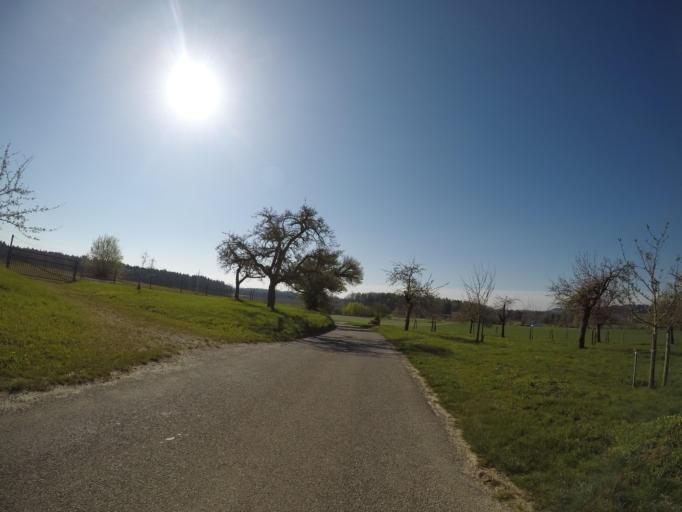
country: DE
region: Baden-Wuerttemberg
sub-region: Tuebingen Region
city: Ebenweiler
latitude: 47.8930
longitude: 9.5235
